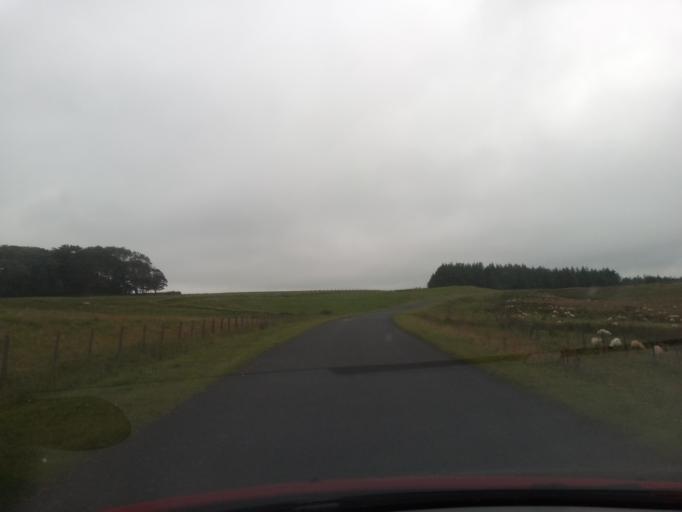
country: GB
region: England
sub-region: Northumberland
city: Otterburn
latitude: 55.2661
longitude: -2.1124
